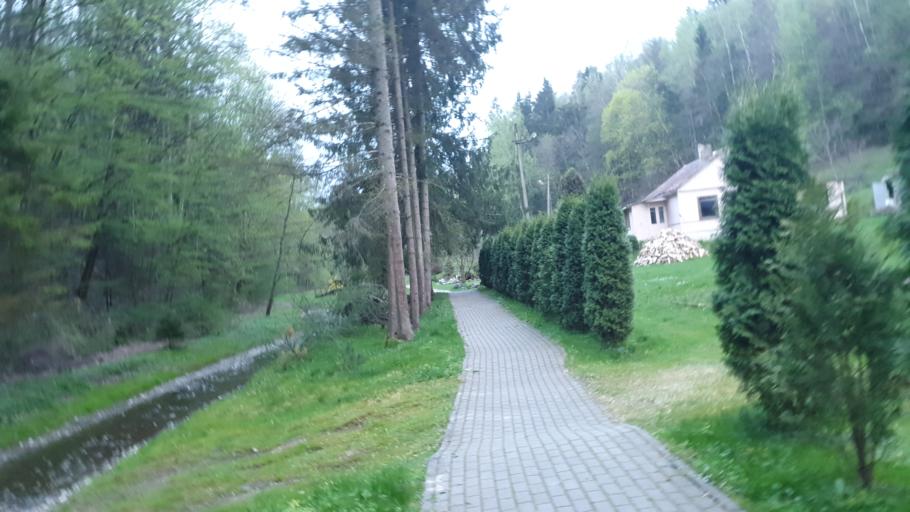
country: LT
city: Sakiai
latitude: 55.0807
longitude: 23.1783
